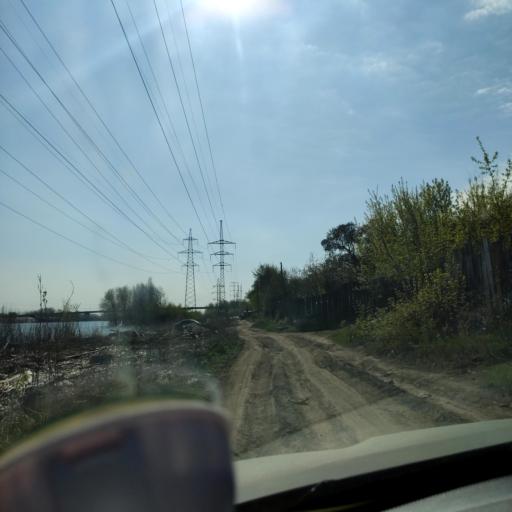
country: RU
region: Samara
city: Samara
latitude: 53.1733
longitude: 50.2070
